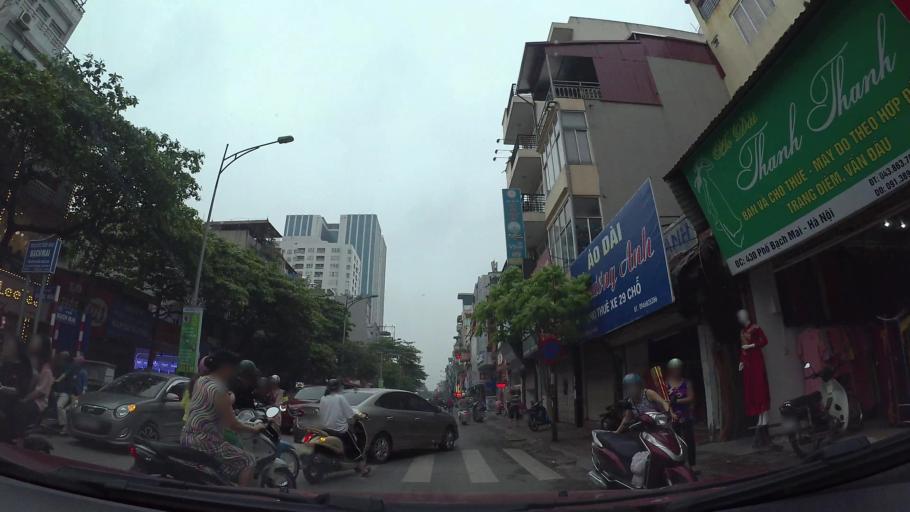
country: VN
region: Ha Noi
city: Hai BaTrung
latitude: 20.9988
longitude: 105.8503
